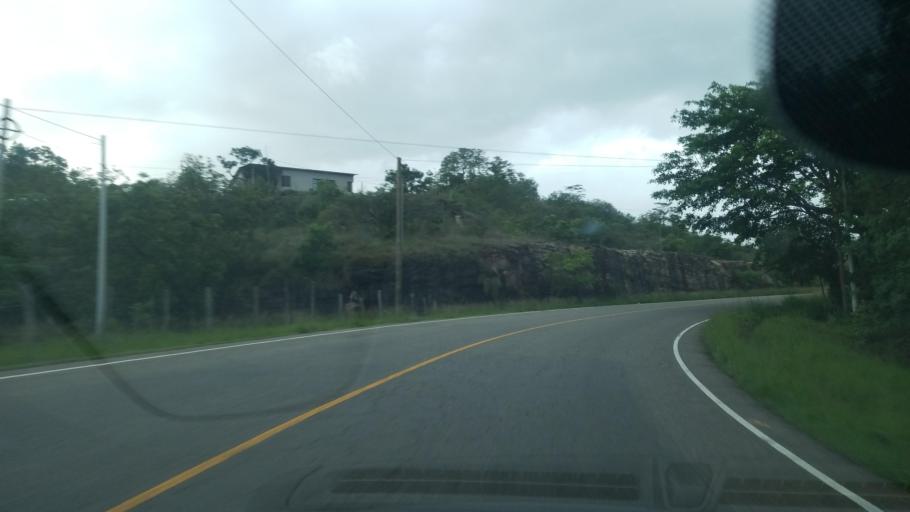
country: HN
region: Ocotepeque
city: Sinuapa
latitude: 14.5206
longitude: -89.2460
